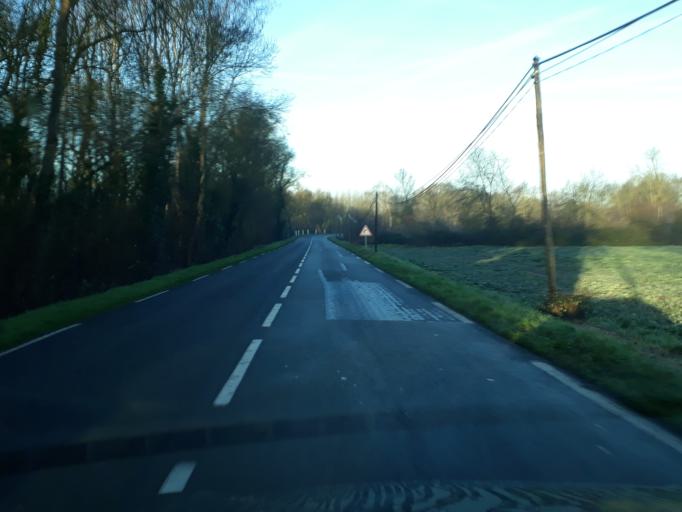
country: FR
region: Midi-Pyrenees
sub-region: Departement de la Haute-Garonne
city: Longages
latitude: 43.3577
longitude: 1.2166
